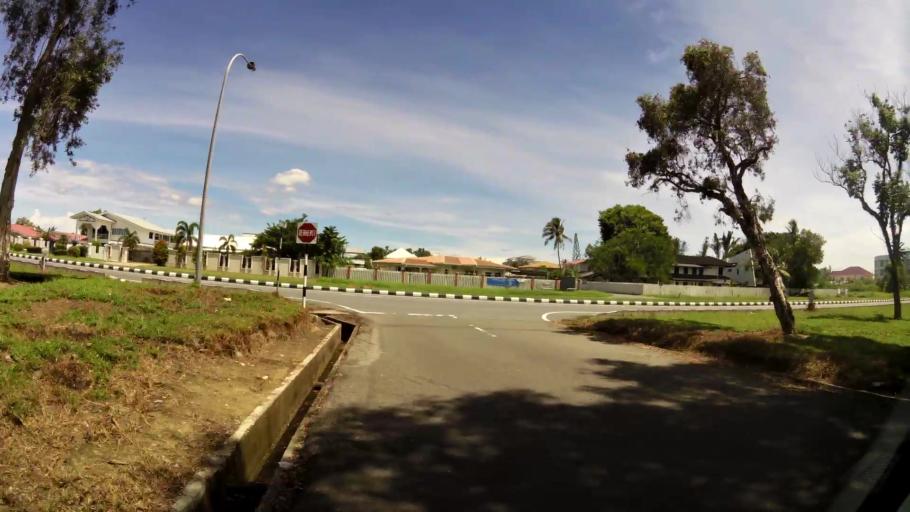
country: BN
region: Belait
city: Kuala Belait
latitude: 4.5946
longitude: 114.2406
